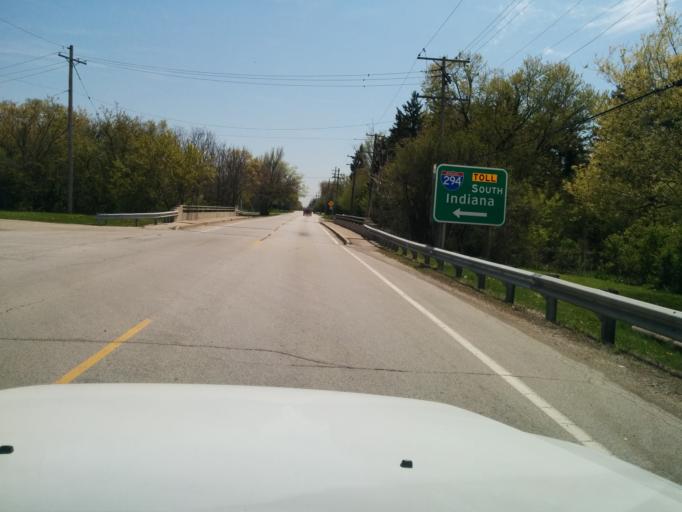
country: US
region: Illinois
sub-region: Cook County
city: Indian Head Park
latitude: 41.7605
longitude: -87.8966
